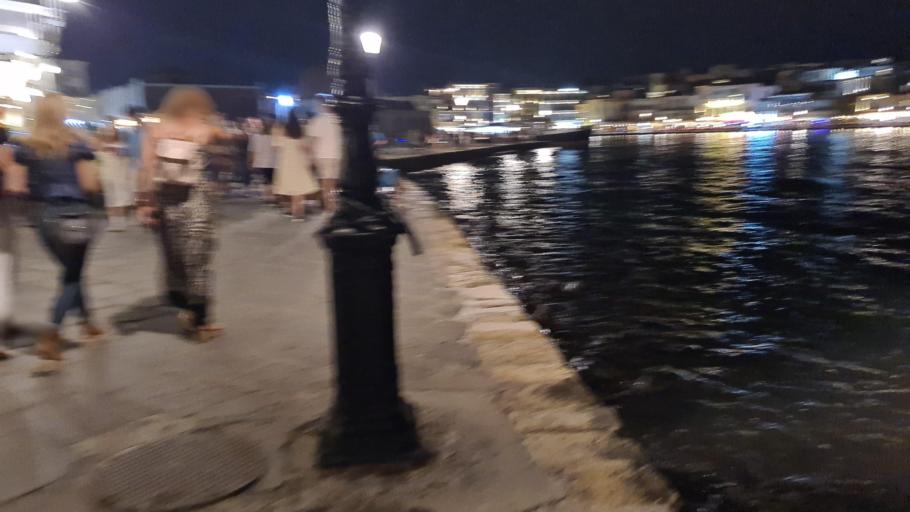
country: GR
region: Crete
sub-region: Nomos Chanias
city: Chania
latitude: 35.5183
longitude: 24.0185
